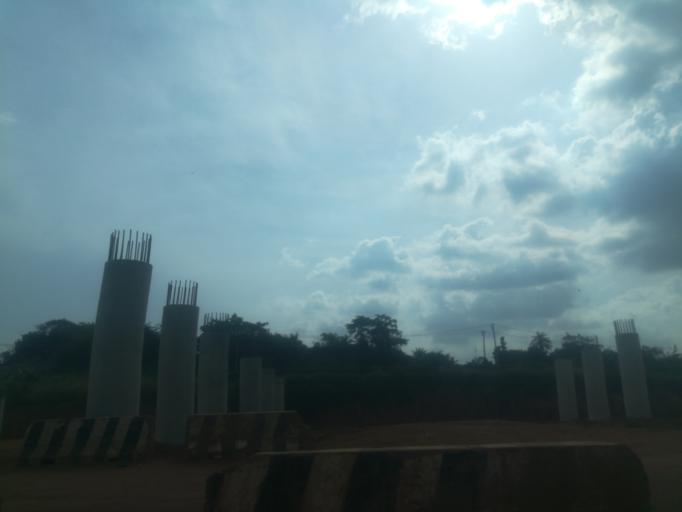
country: NG
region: Ogun
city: Abeokuta
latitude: 7.1343
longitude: 3.3520
